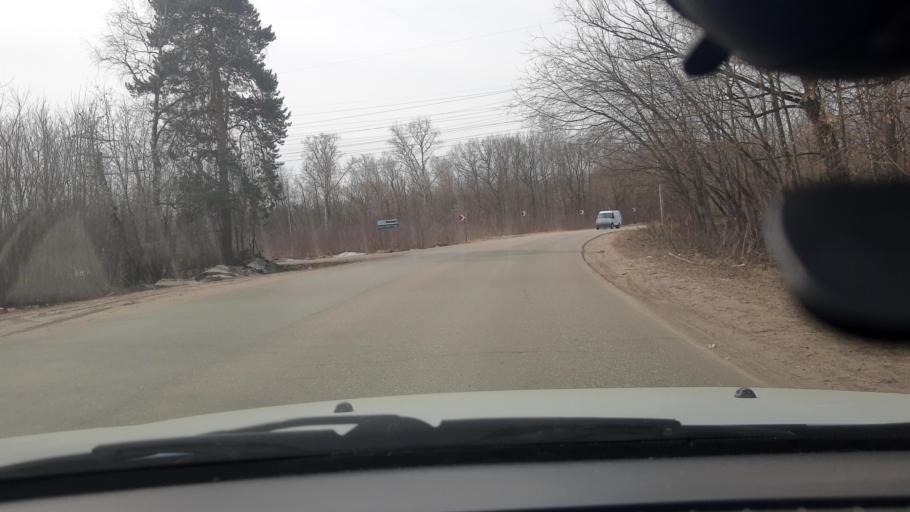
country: RU
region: Nizjnij Novgorod
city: Gidrotorf
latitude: 56.4738
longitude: 43.5642
